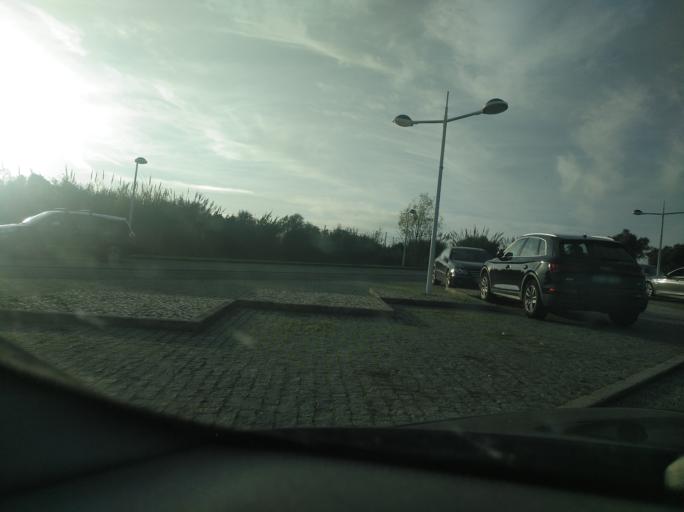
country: PT
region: Lisbon
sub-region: Odivelas
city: Olival do Basto
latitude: 38.7755
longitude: -9.1712
